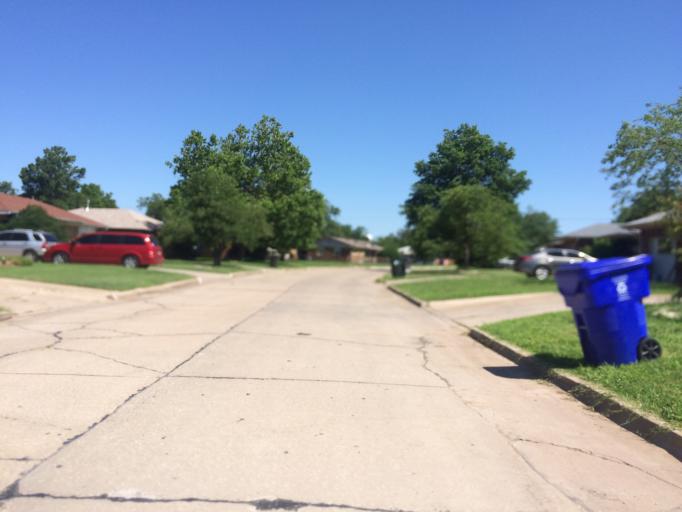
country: US
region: Oklahoma
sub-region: Cleveland County
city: Norman
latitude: 35.2309
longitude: -97.4568
